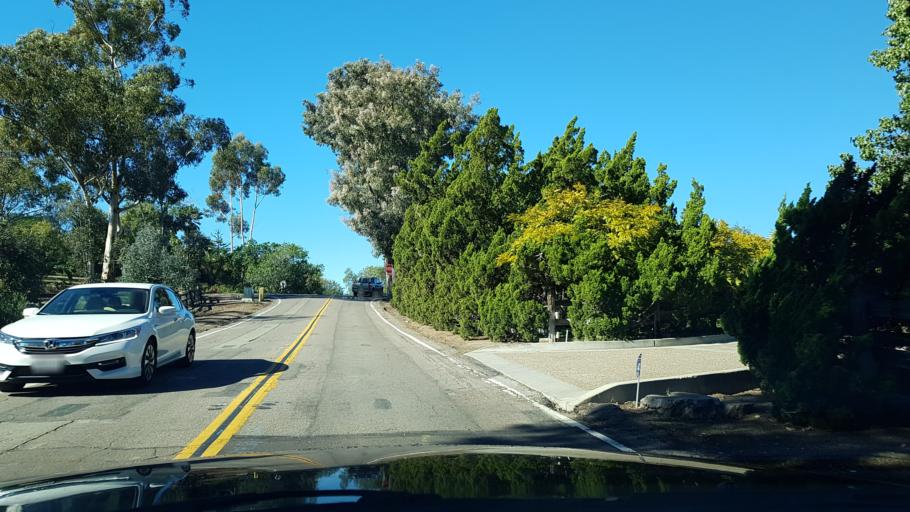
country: US
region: California
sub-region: San Diego County
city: Rancho Santa Fe
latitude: 33.0389
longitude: -117.2101
